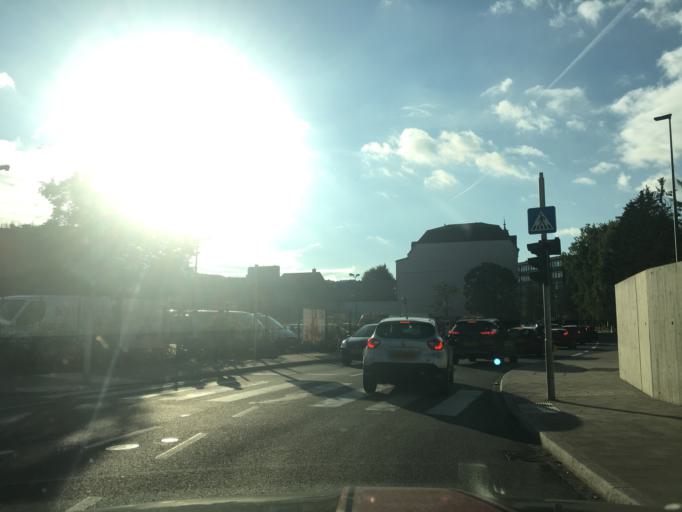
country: LU
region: Luxembourg
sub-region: Canton d'Esch-sur-Alzette
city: Differdange
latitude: 49.5225
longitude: 5.8969
